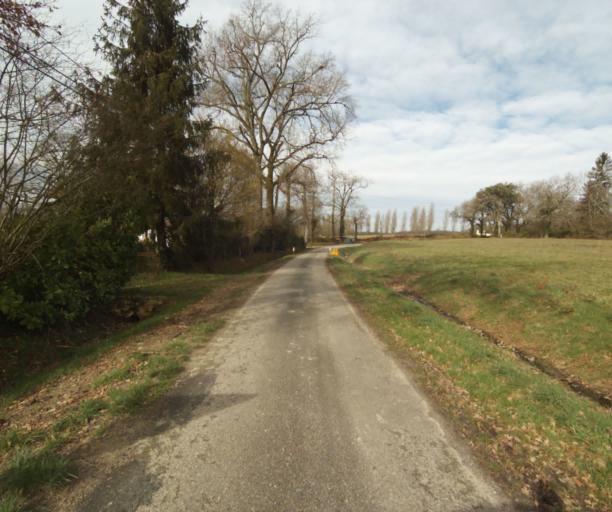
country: FR
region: Aquitaine
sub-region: Departement des Landes
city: Gabarret
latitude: 43.9703
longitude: 0.0047
